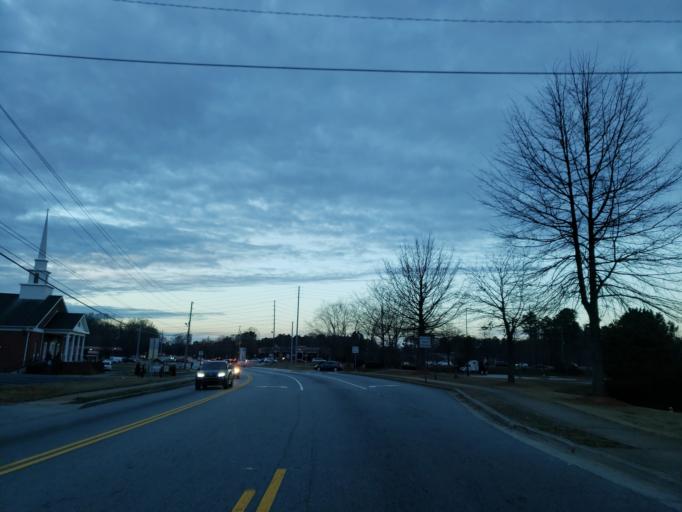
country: US
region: Georgia
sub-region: Cobb County
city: Mableton
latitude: 33.8549
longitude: -84.5889
